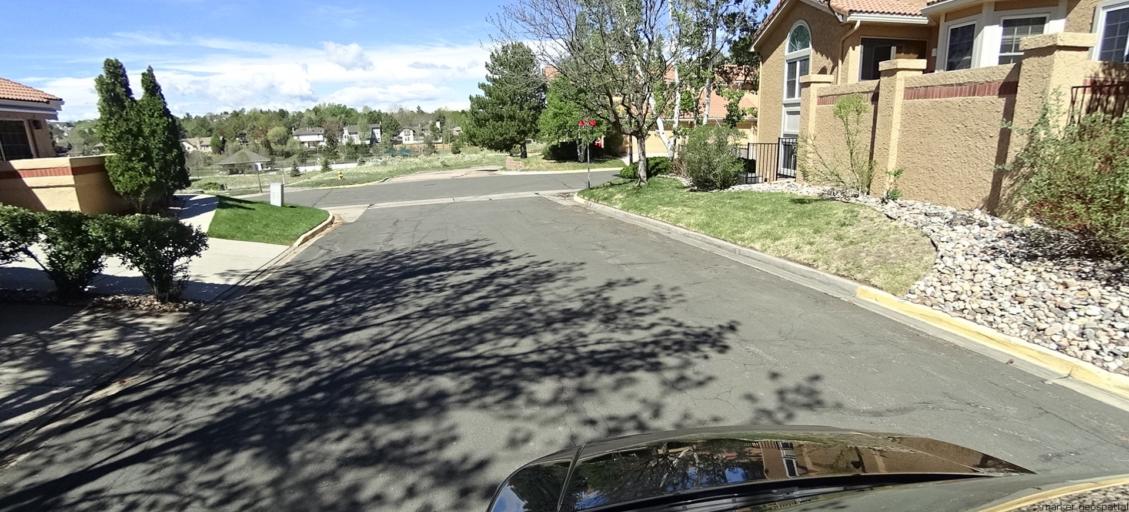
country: US
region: Colorado
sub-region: Adams County
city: Lone Tree
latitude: 39.5496
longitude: -104.8870
